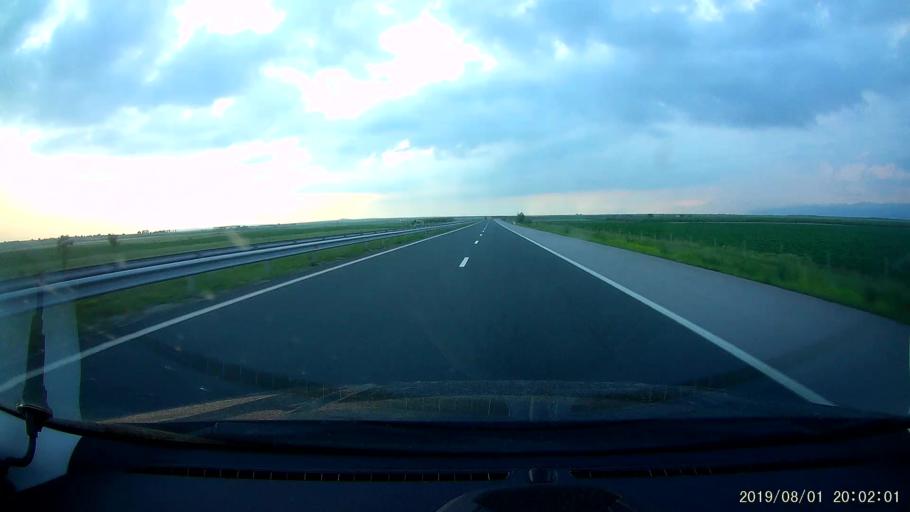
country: BG
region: Yambol
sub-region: Obshtina Straldzha
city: Straldzha
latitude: 42.5579
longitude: 26.6446
